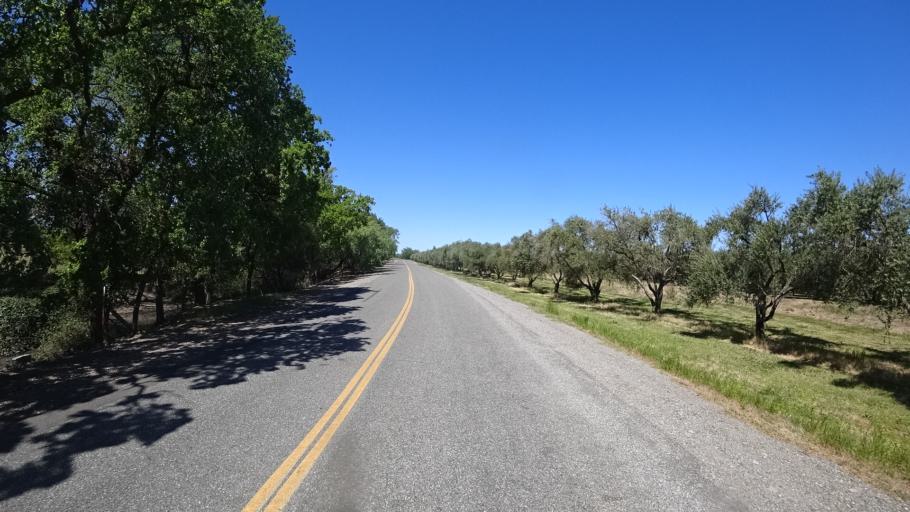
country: US
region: California
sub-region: Glenn County
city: Orland
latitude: 39.7856
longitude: -122.2181
